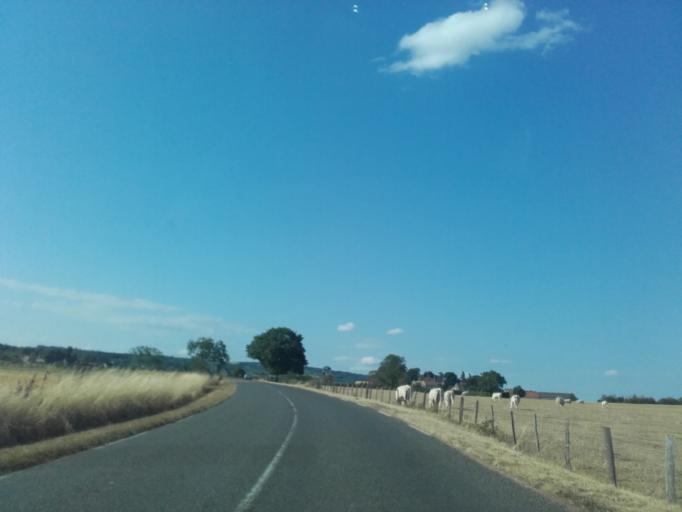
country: FR
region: Bourgogne
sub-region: Departement de Saone-et-Loire
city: Buxy
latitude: 46.7419
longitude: 4.7126
